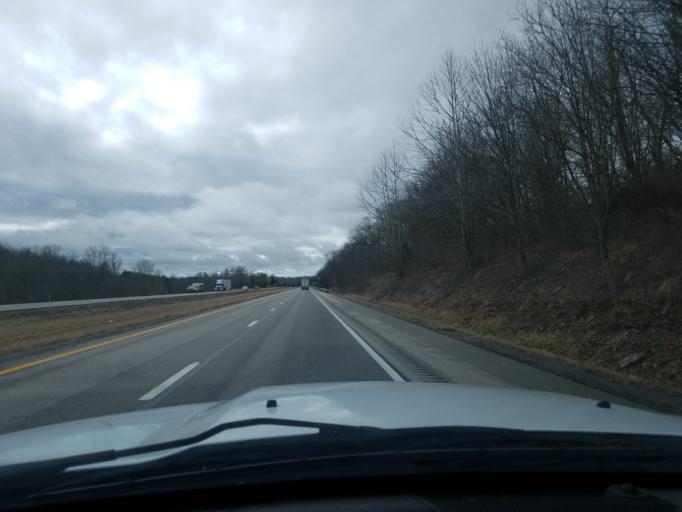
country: US
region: Kentucky
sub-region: Montgomery County
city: Mount Sterling
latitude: 38.0522
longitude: -84.0569
